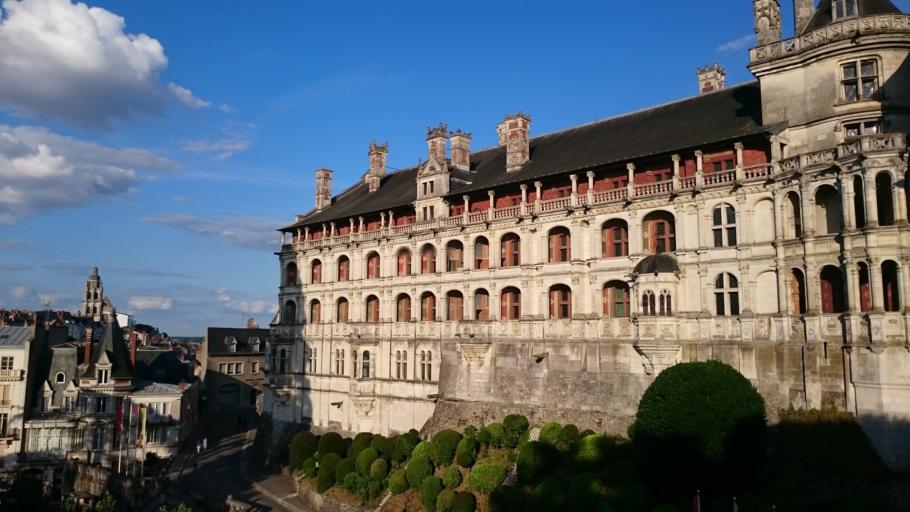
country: FR
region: Centre
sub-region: Departement du Loir-et-Cher
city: Blois
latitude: 47.5859
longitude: 1.3298
